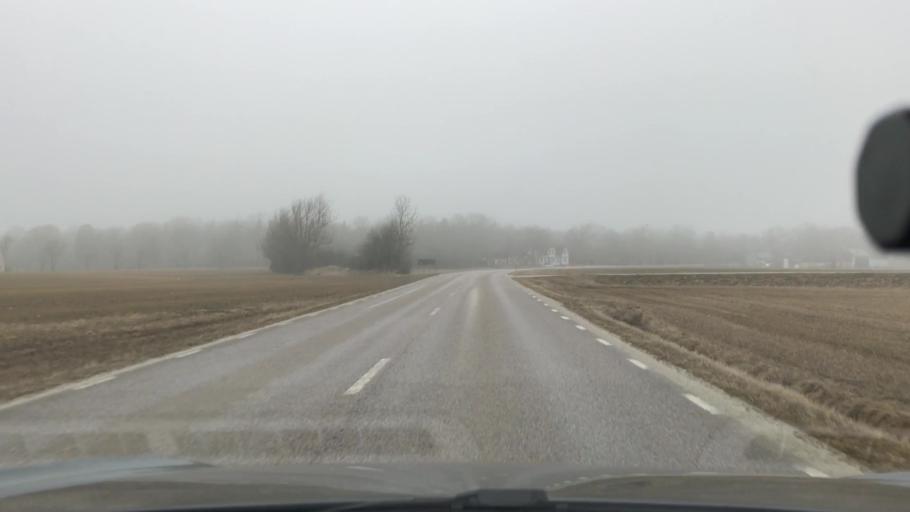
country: SE
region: Gotland
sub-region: Gotland
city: Hemse
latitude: 57.3068
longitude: 18.3804
